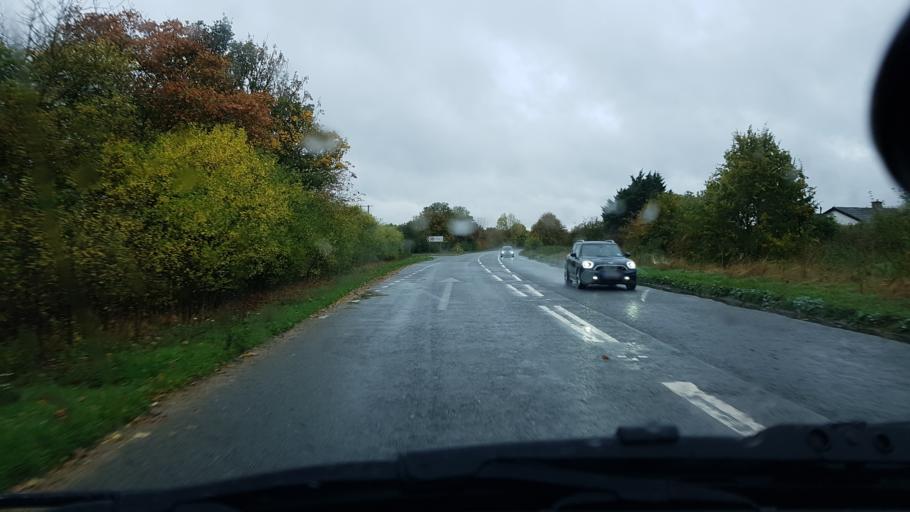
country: GB
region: England
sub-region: Oxfordshire
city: Ducklington
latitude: 51.7662
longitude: -1.4880
